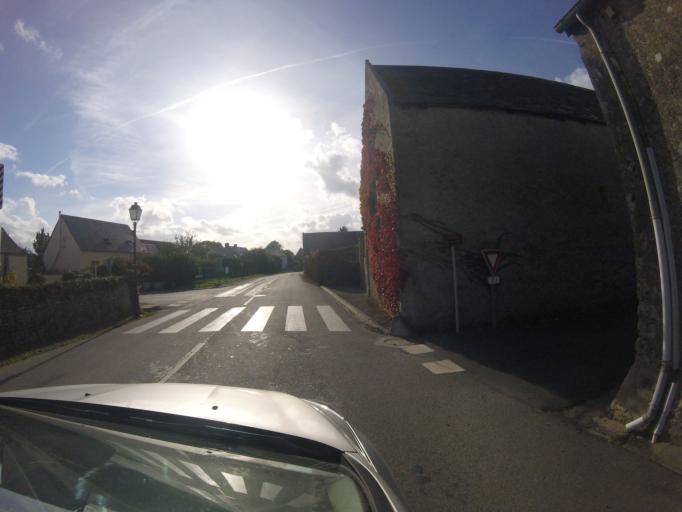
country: FR
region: Lower Normandy
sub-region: Departement du Calvados
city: Port-en-Bessin-Huppain
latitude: 49.3489
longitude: -0.8408
